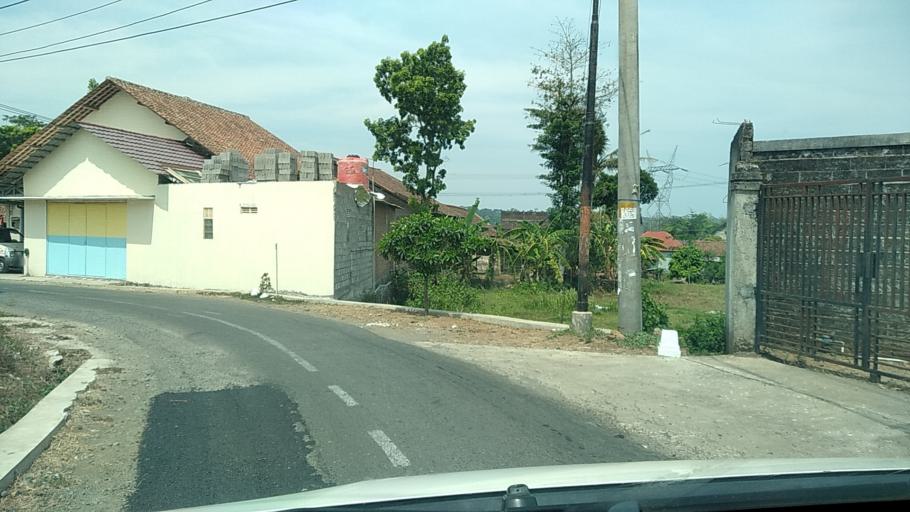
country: ID
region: Central Java
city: Ungaran
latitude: -7.0752
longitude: 110.3342
